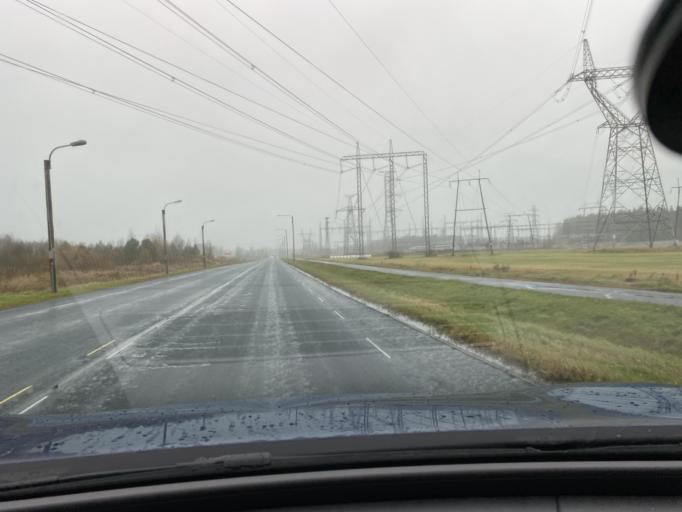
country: FI
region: Haeme
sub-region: Forssa
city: Forssa
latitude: 60.8008
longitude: 23.5811
